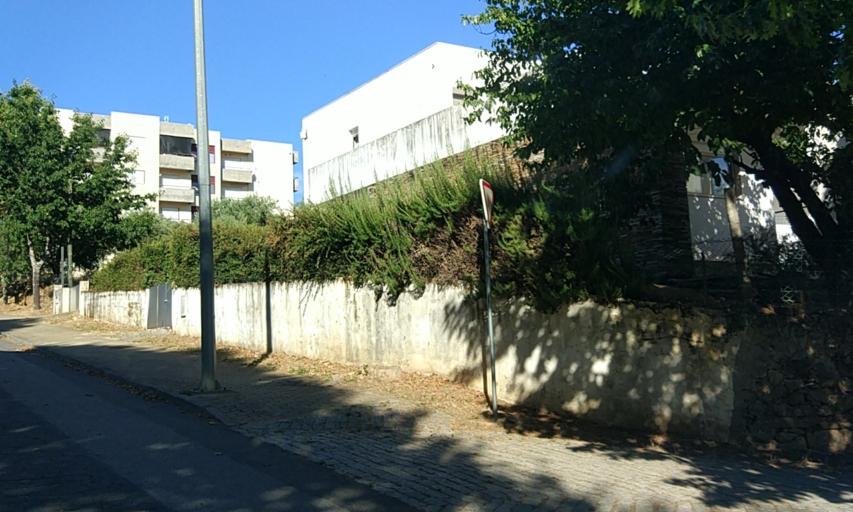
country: PT
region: Vila Real
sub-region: Murca
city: Murca
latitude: 41.4026
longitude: -7.4565
